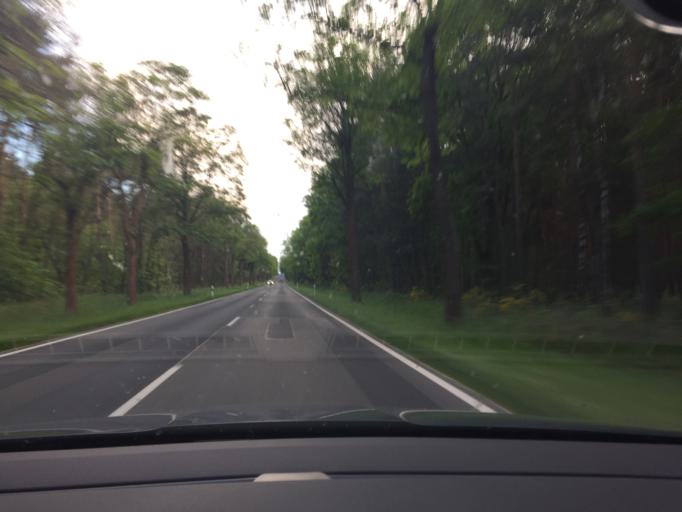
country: DE
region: Brandenburg
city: Treuenbrietzen
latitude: 52.0588
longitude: 12.8231
